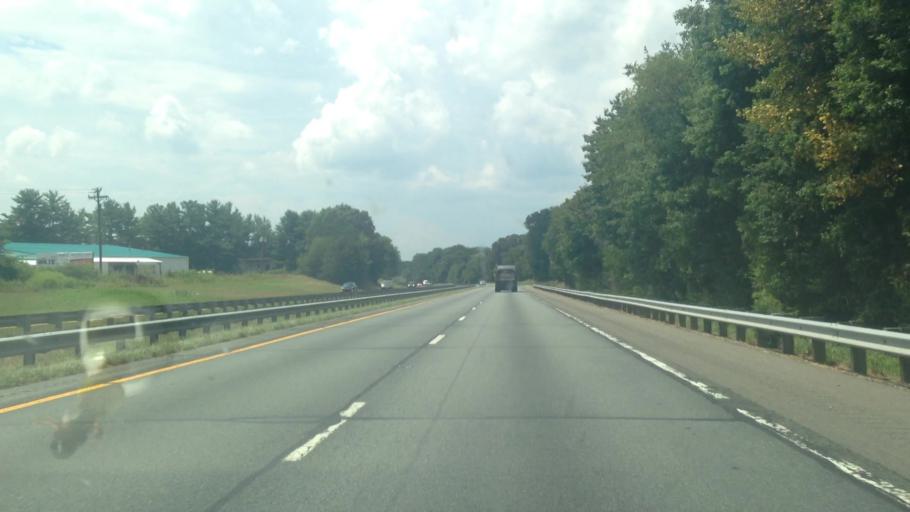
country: US
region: North Carolina
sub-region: Stokes County
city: King
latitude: 36.2729
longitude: -80.3773
